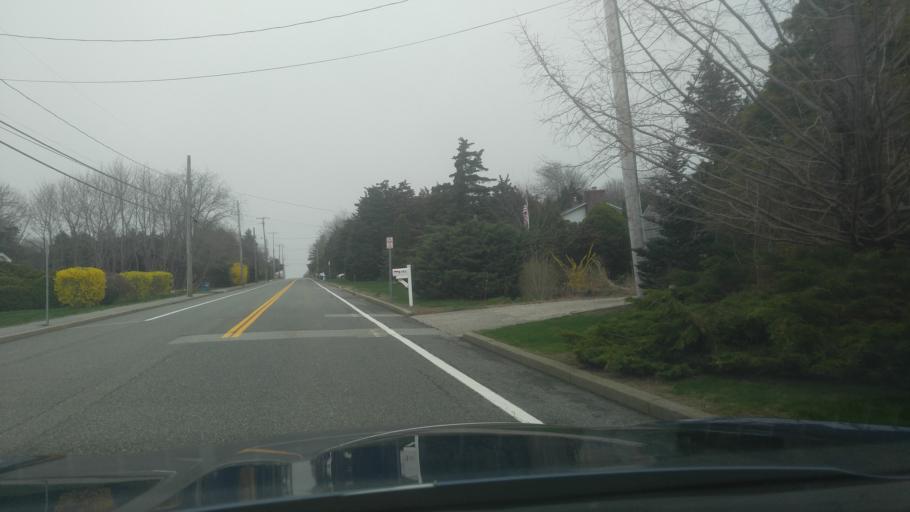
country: US
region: Rhode Island
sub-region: Newport County
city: Jamestown
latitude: 41.4890
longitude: -71.3779
